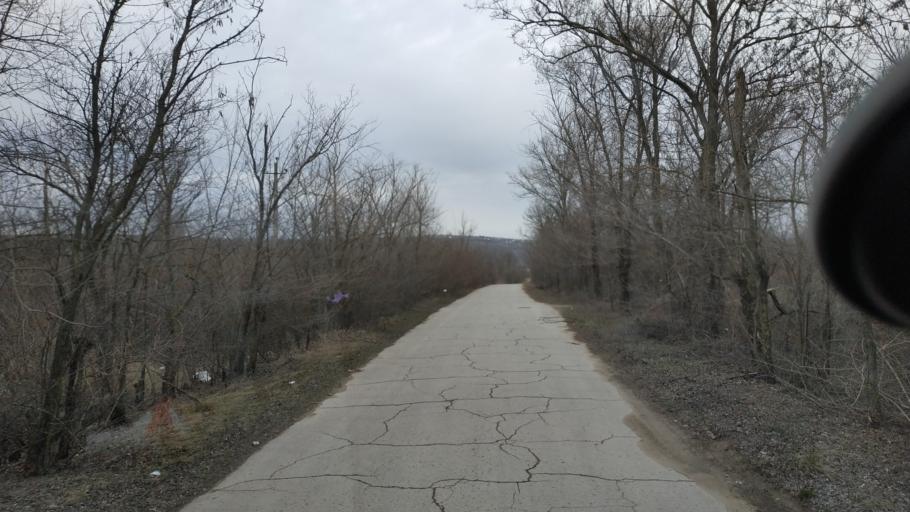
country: MD
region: Telenesti
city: Cocieri
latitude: 47.3291
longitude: 29.0910
